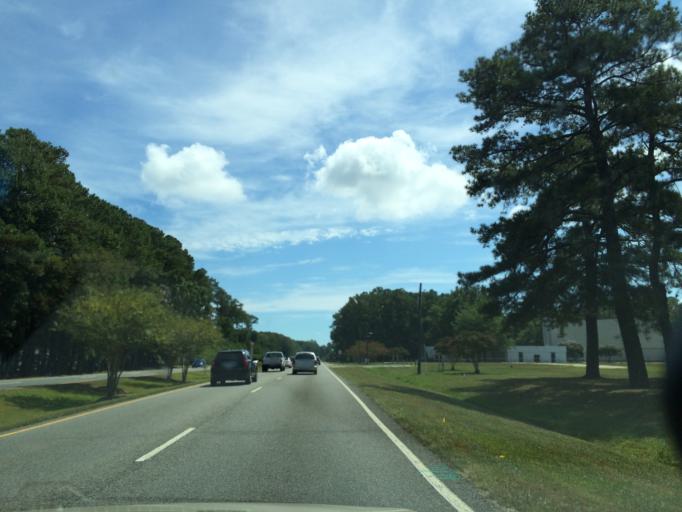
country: US
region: Virginia
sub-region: York County
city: Yorktown
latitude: 37.2018
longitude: -76.5002
